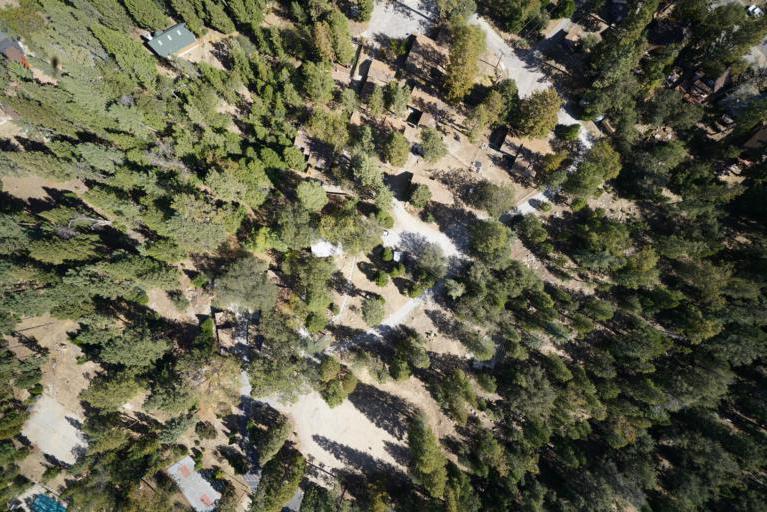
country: US
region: California
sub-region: Riverside County
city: Idyllwild
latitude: 33.7507
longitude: -116.7003
